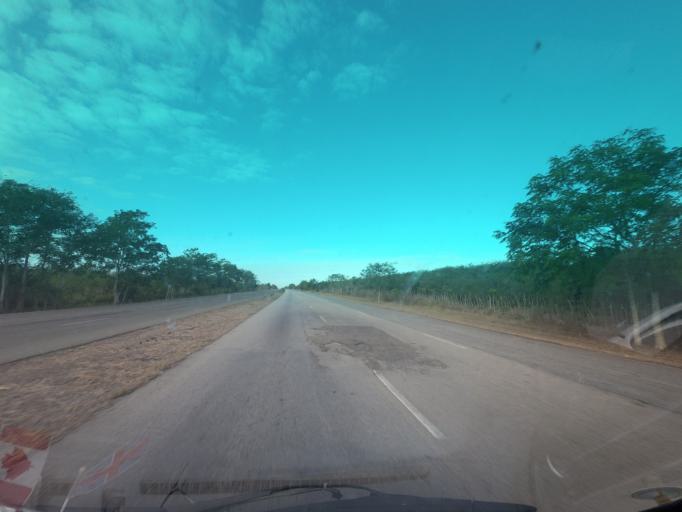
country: CU
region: Cienfuegos
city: Rodas
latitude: 22.4447
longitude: -80.4234
